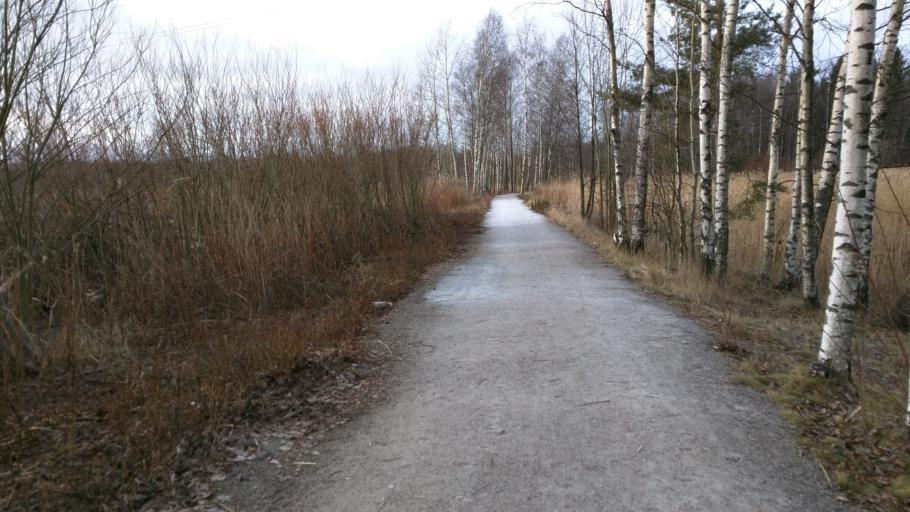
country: FI
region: Uusimaa
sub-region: Helsinki
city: Koukkuniemi
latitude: 60.1543
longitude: 24.7207
